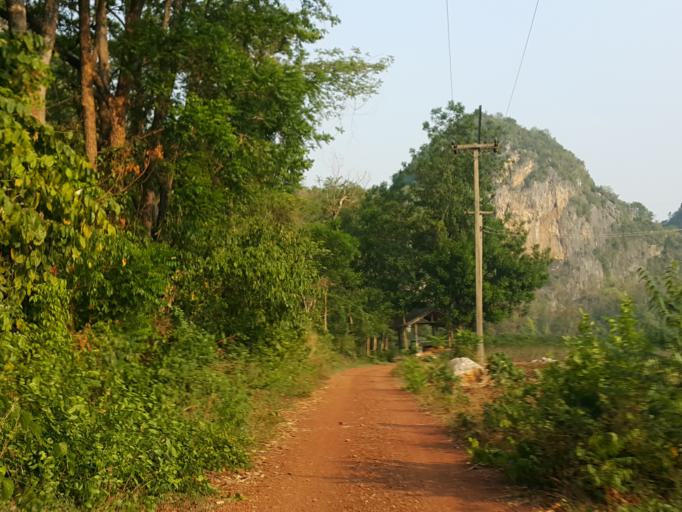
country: TH
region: Uthai Thani
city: Huai Khot
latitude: 15.3263
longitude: 99.6771
